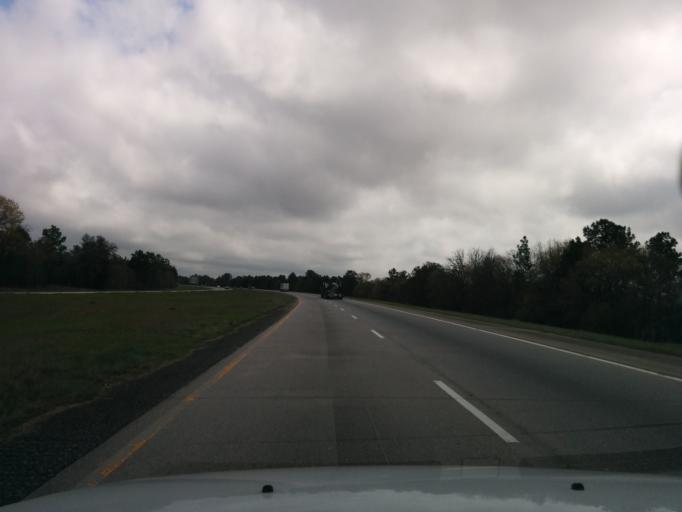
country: US
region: Georgia
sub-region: Toombs County
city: Lyons
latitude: 32.3921
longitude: -82.2930
